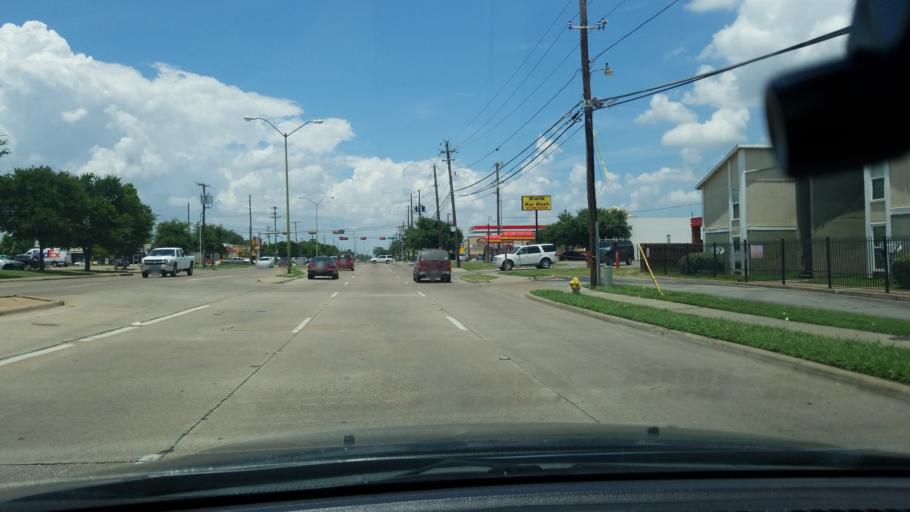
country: US
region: Texas
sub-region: Dallas County
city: Balch Springs
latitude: 32.7327
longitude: -96.6483
